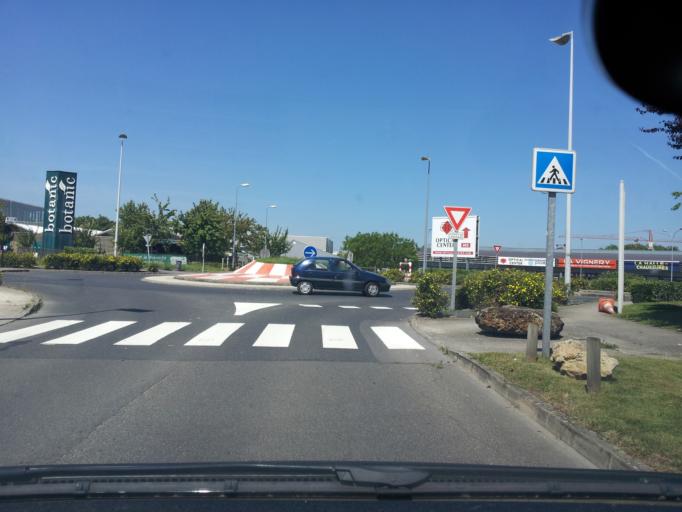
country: FR
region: Ile-de-France
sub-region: Departement de l'Essonne
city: Marolles-en-Hurepoix
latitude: 48.5865
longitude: 2.3008
